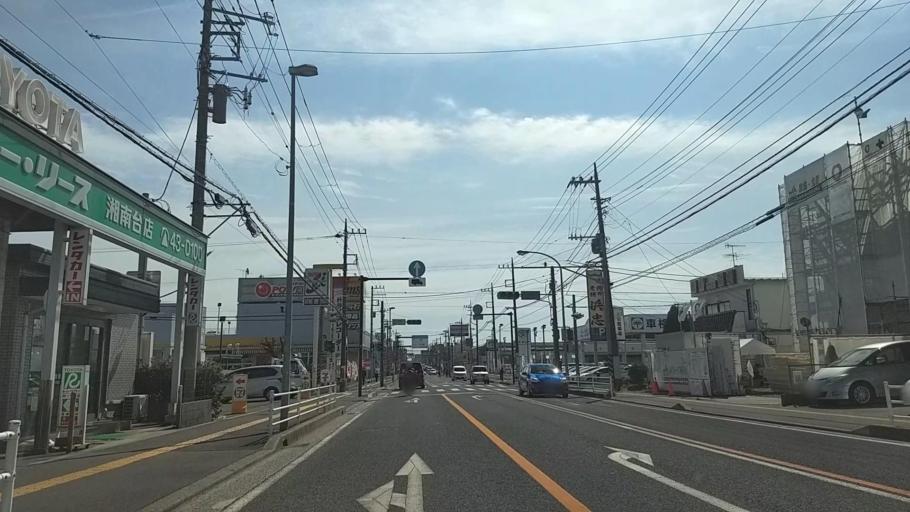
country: JP
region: Kanagawa
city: Fujisawa
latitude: 35.3952
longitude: 139.4710
